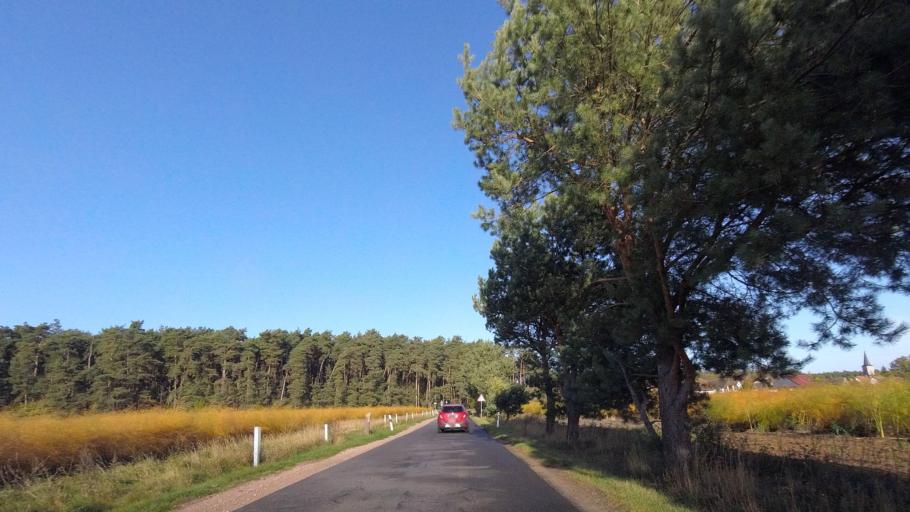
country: DE
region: Brandenburg
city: Borkheide
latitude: 52.2058
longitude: 12.8983
